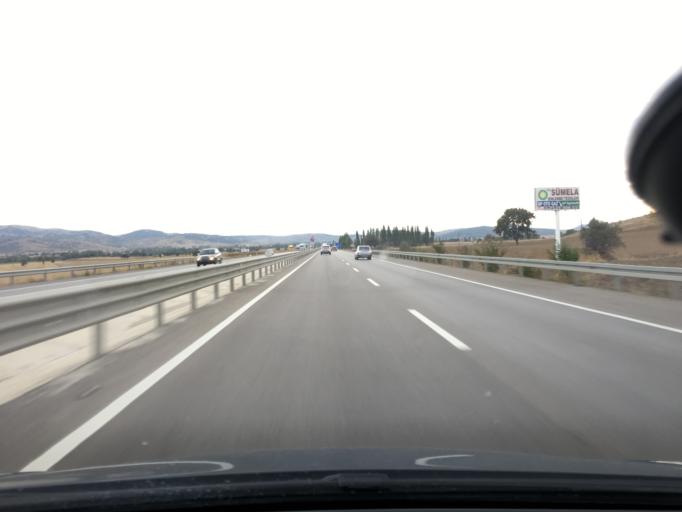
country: TR
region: Afyonkarahisar
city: Sincanli
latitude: 38.6417
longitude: 30.3074
